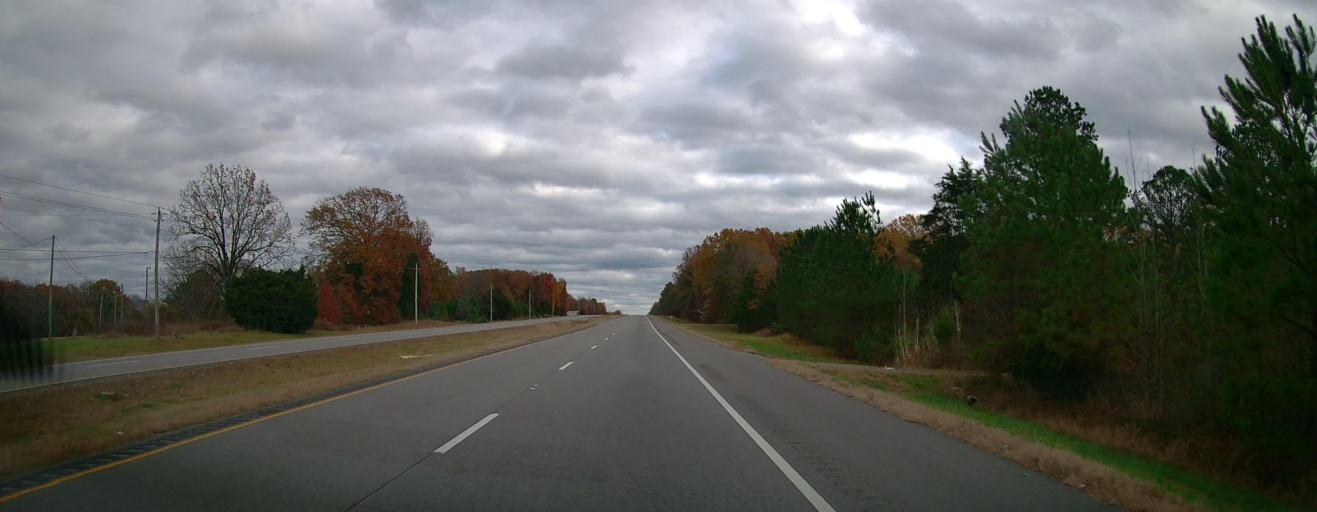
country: US
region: Alabama
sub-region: Colbert County
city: Muscle Shoals
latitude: 34.6700
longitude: -87.5611
